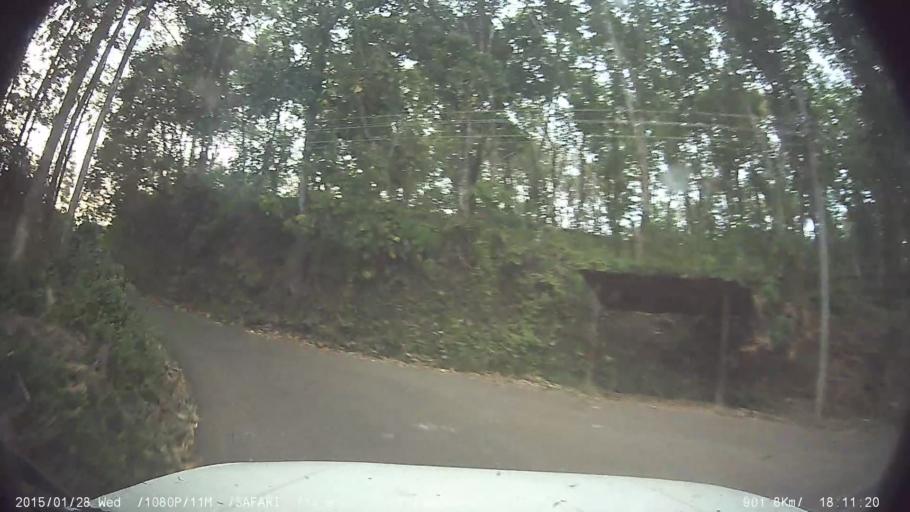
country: IN
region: Kerala
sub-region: Kottayam
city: Palackattumala
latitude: 9.7513
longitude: 76.5694
